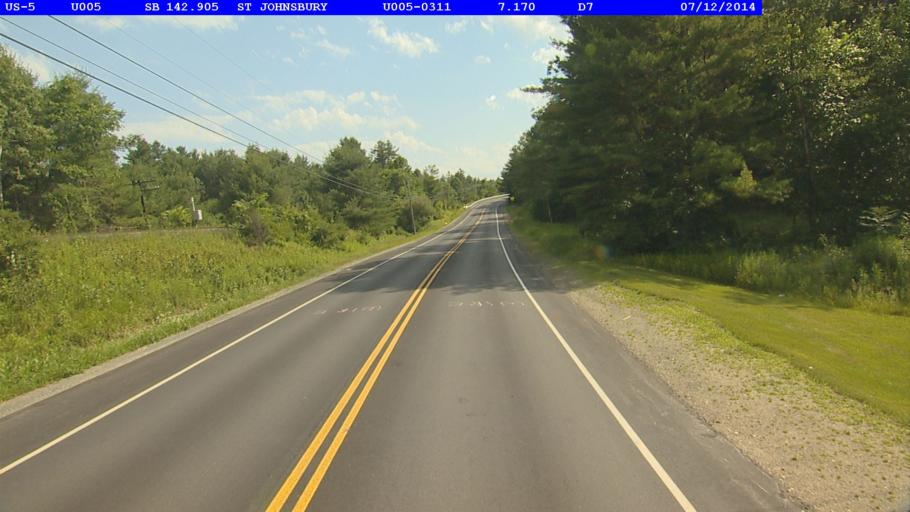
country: US
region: Vermont
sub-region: Caledonia County
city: Lyndon
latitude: 44.4914
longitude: -72.0056
